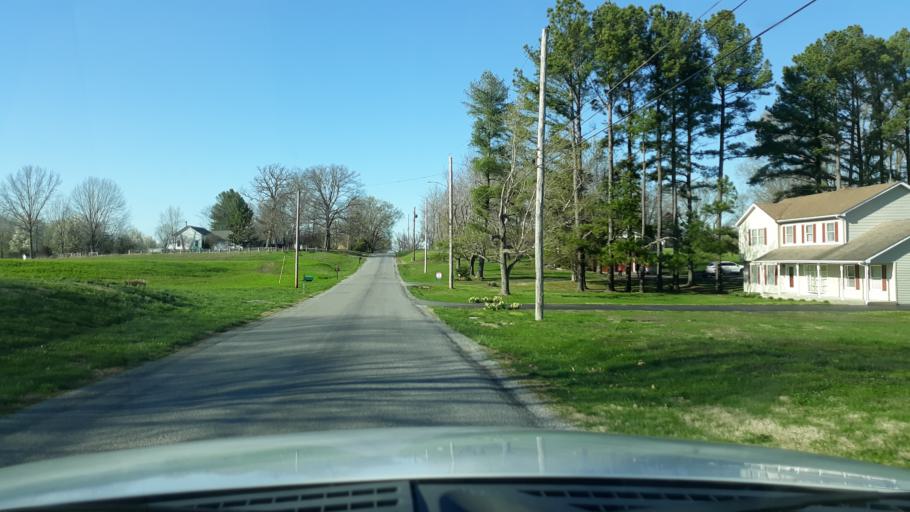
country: US
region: Illinois
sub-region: Saline County
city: Harrisburg
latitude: 37.7503
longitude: -88.5680
